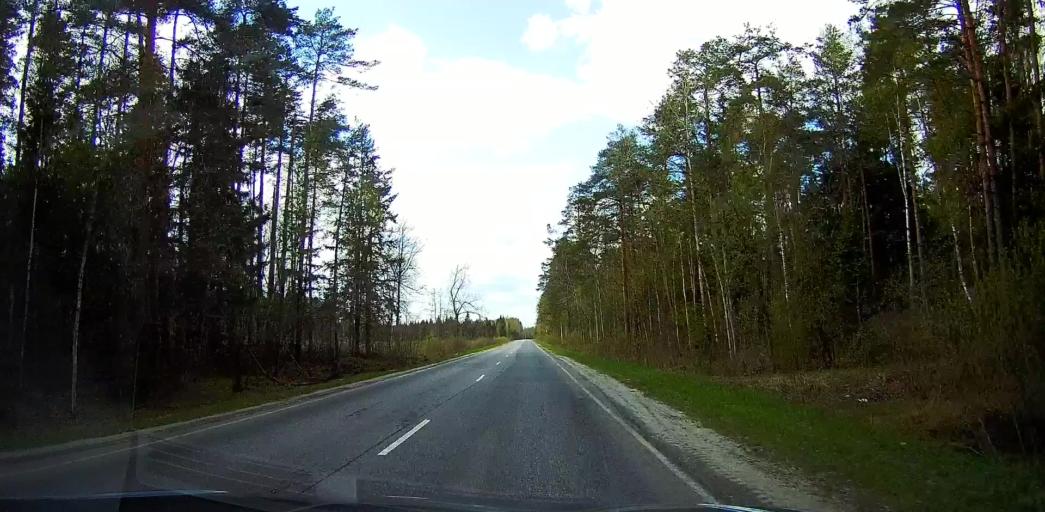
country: RU
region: Moskovskaya
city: Rakhmanovo
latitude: 55.6475
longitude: 38.6709
